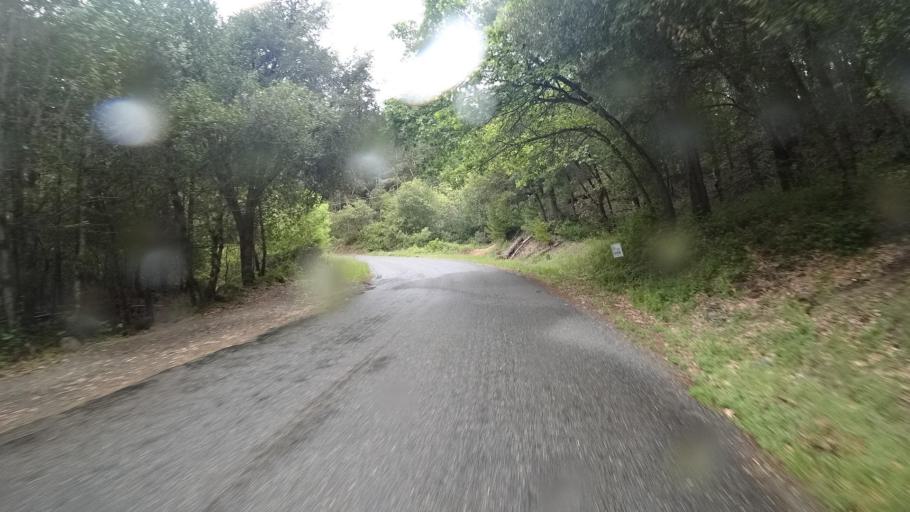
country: US
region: California
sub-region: Siskiyou County
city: Happy Camp
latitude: 41.3721
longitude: -123.5011
